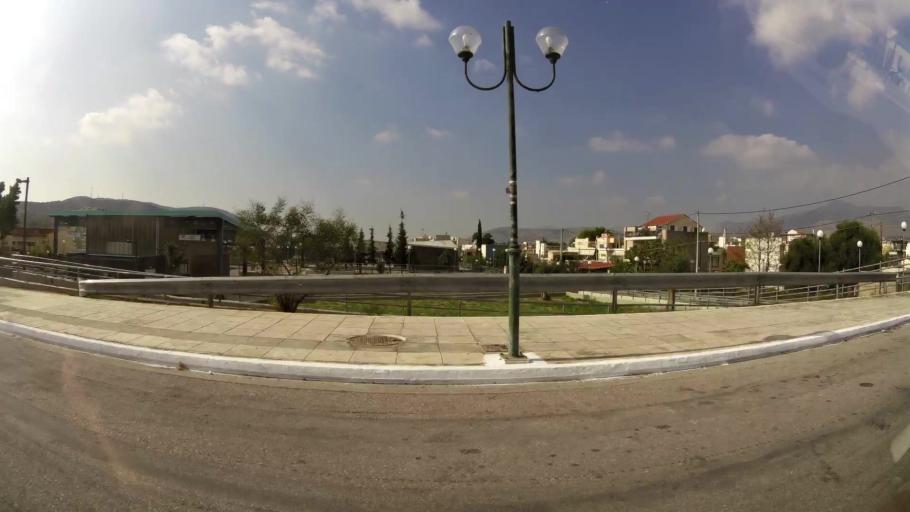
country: GR
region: Attica
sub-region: Nomarchia Dytikis Attikis
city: Zefyri
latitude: 38.0699
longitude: 23.7170
